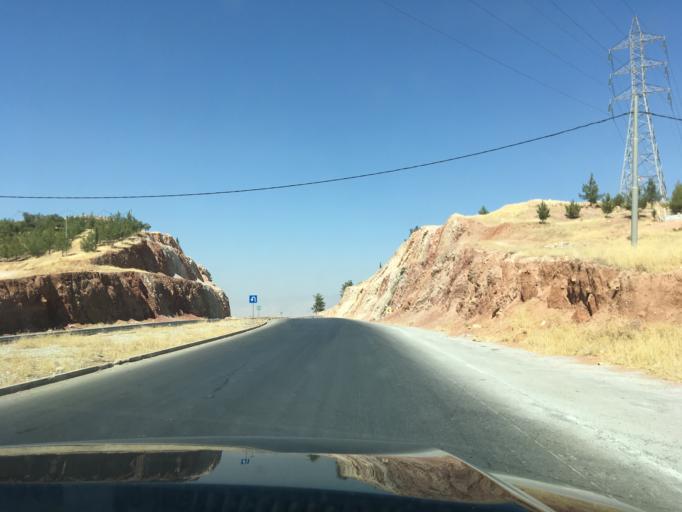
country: IQ
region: Arbil
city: Shaqlawah
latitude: 36.4870
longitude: 44.3810
